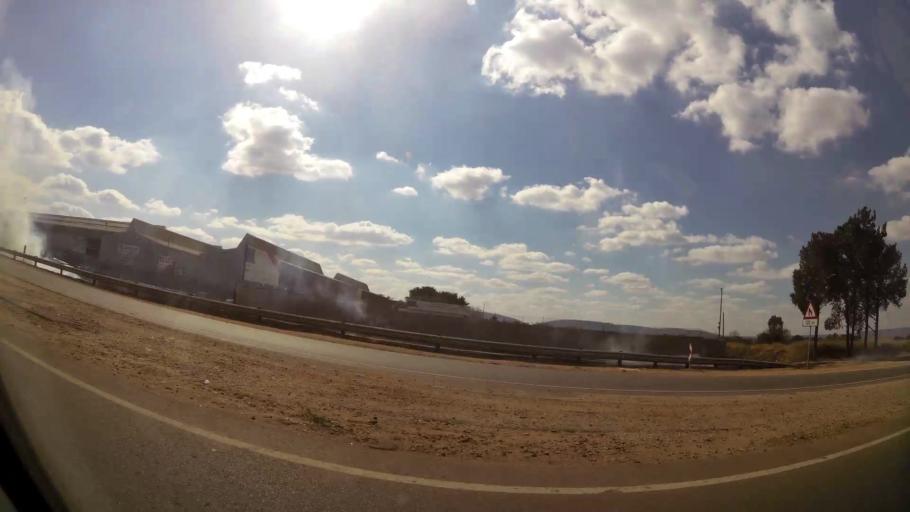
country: ZA
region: Gauteng
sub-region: City of Tshwane Metropolitan Municipality
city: Pretoria
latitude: -25.7388
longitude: 28.3325
